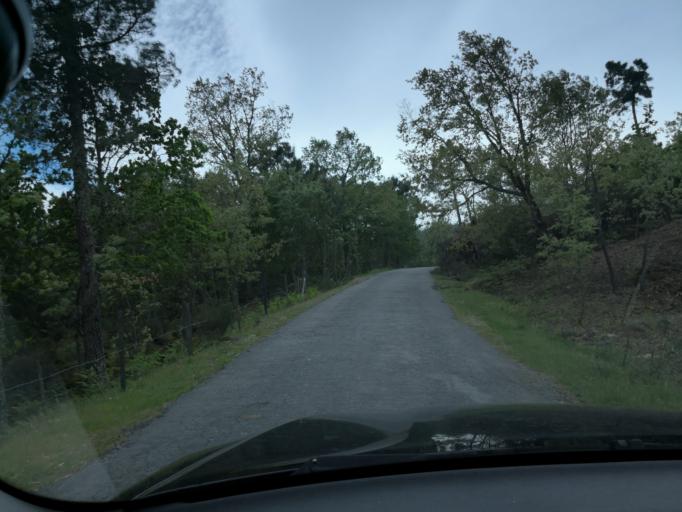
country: PT
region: Vila Real
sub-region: Vila Real
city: Vila Real
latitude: 41.2966
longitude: -7.8025
